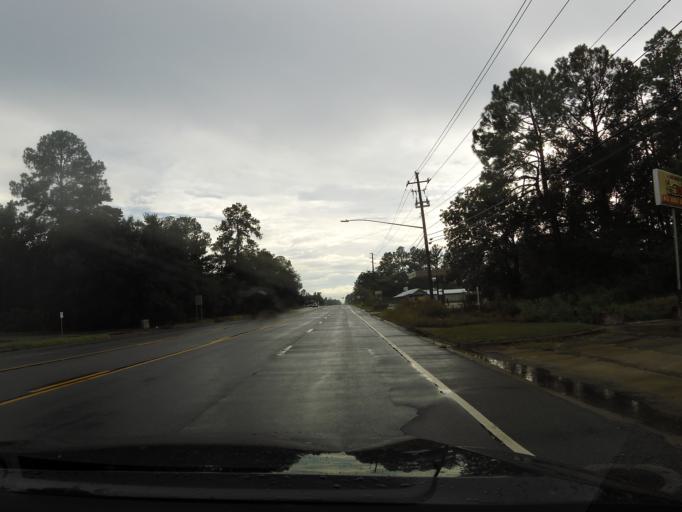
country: US
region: Georgia
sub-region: Wayne County
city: Jesup
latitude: 31.5918
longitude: -81.8721
